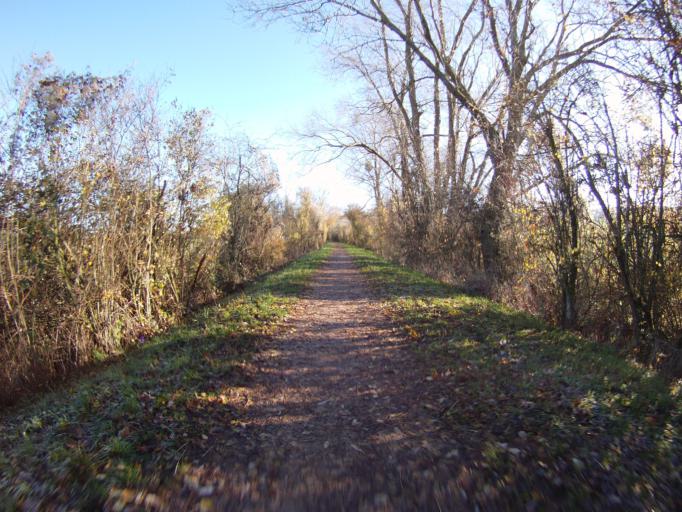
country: FR
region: Lorraine
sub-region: Departement de Meurthe-et-Moselle
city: Faulx
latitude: 48.7916
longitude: 6.2190
